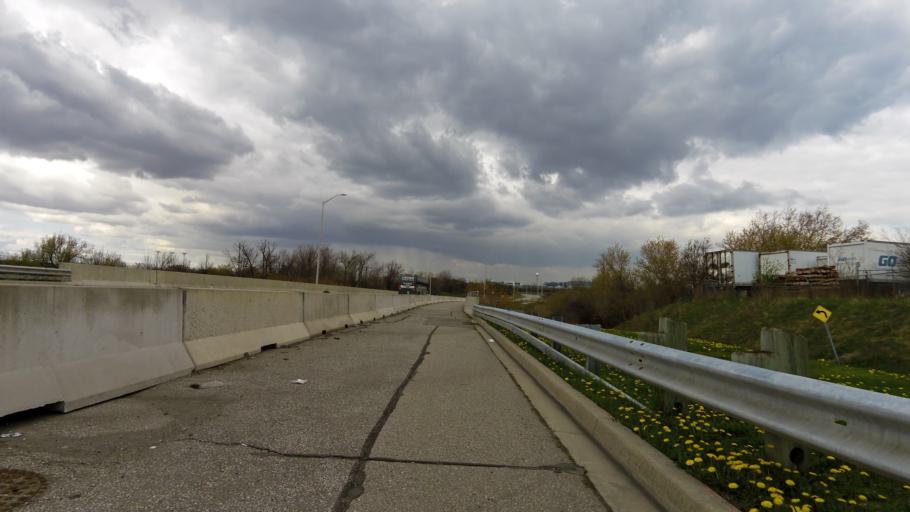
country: CA
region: Ontario
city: Etobicoke
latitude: 43.6724
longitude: -79.6480
